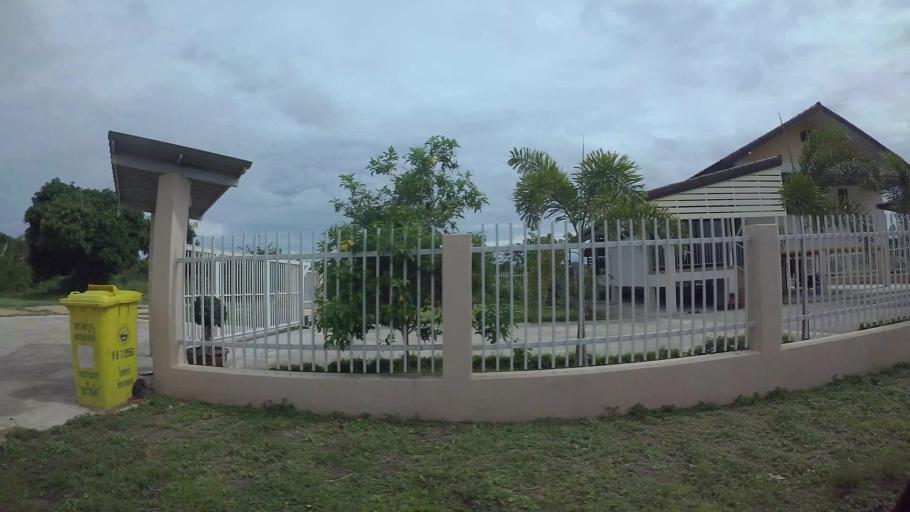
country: TH
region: Chon Buri
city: Sattahip
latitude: 12.7132
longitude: 100.9018
